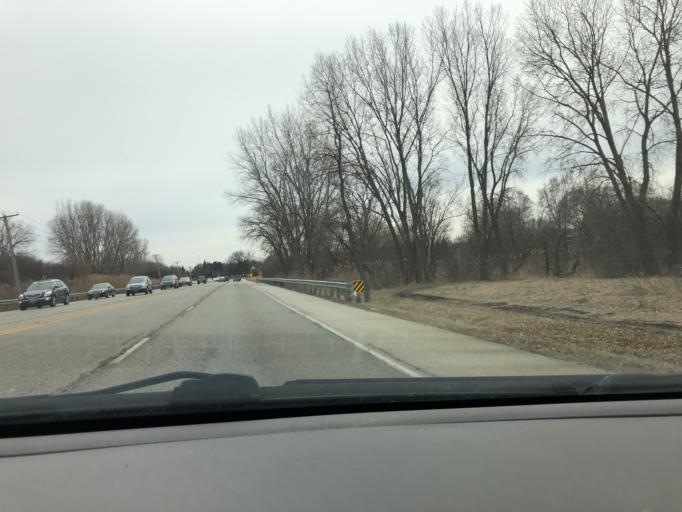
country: US
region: Illinois
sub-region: Kane County
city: Elgin
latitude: 42.0406
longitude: -88.3413
